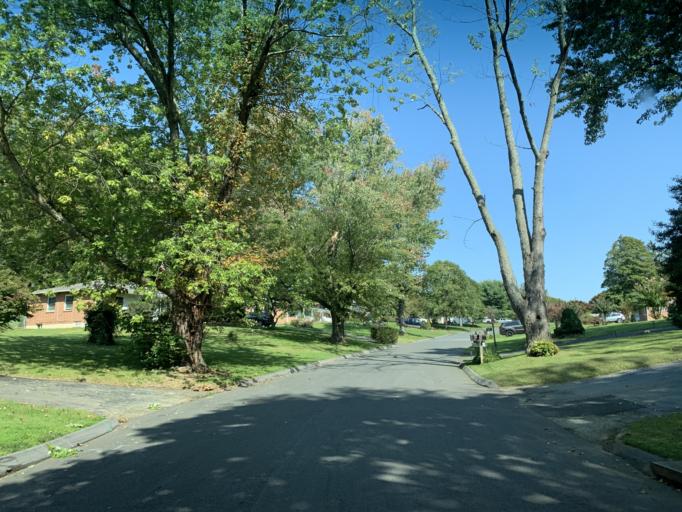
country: US
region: Maryland
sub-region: Harford County
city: South Bel Air
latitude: 39.5218
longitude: -76.3423
